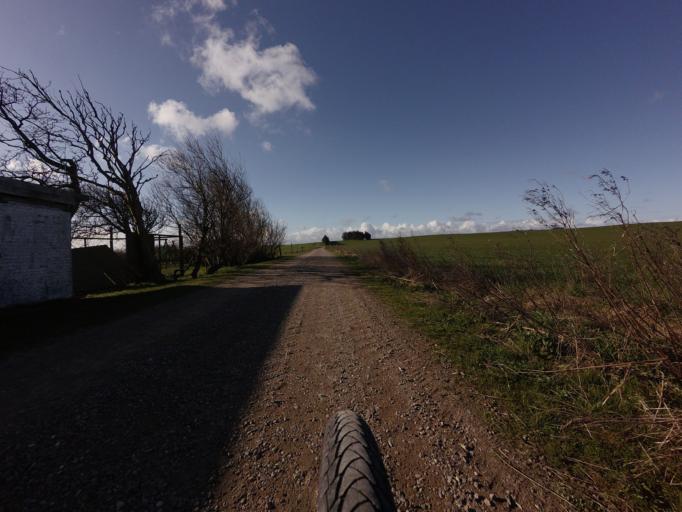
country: DK
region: North Denmark
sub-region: Hjorring Kommune
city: Vra
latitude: 57.3699
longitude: 9.8144
